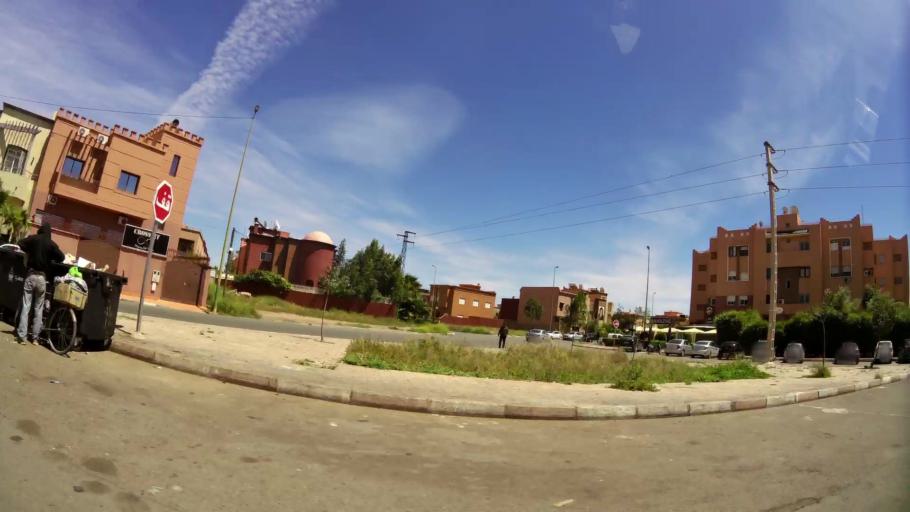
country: MA
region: Marrakech-Tensift-Al Haouz
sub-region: Marrakech
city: Marrakesh
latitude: 31.6414
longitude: -8.0463
